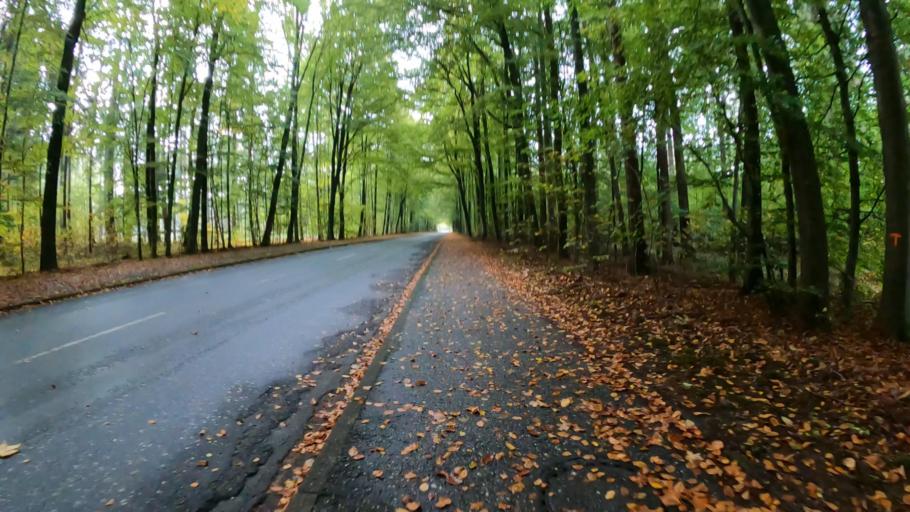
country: DE
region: Schleswig-Holstein
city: Ahrensburg
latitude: 53.6507
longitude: 10.2288
